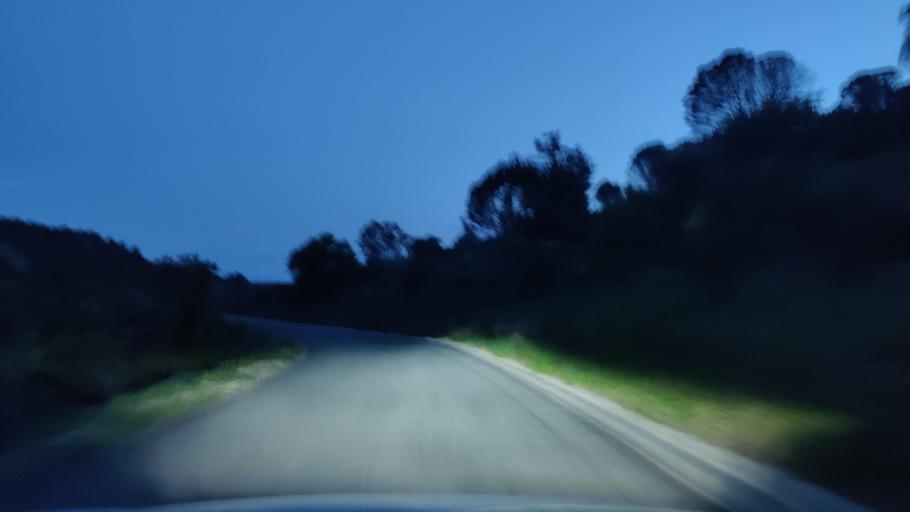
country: FR
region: Languedoc-Roussillon
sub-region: Departement des Pyrenees-Orientales
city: Estagel
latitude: 42.8823
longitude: 2.7466
